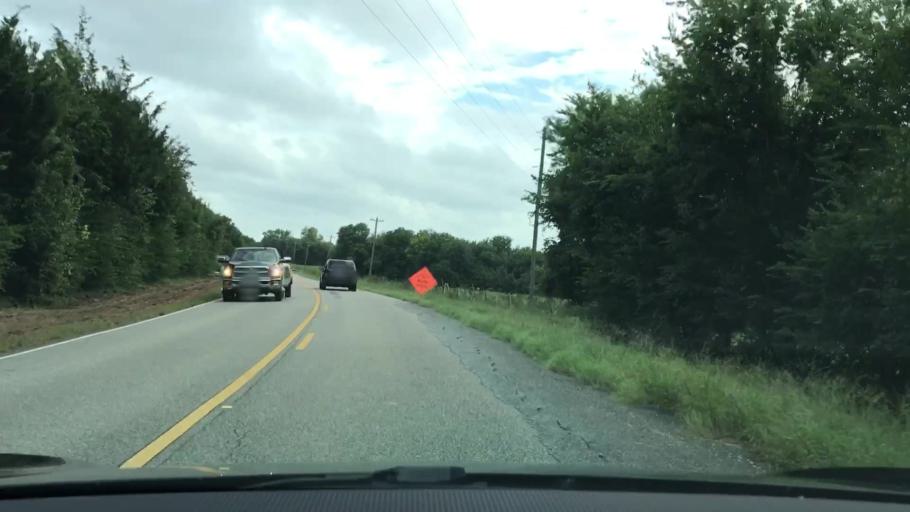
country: US
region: Alabama
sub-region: Montgomery County
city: Pike Road
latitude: 32.2898
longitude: -86.0763
